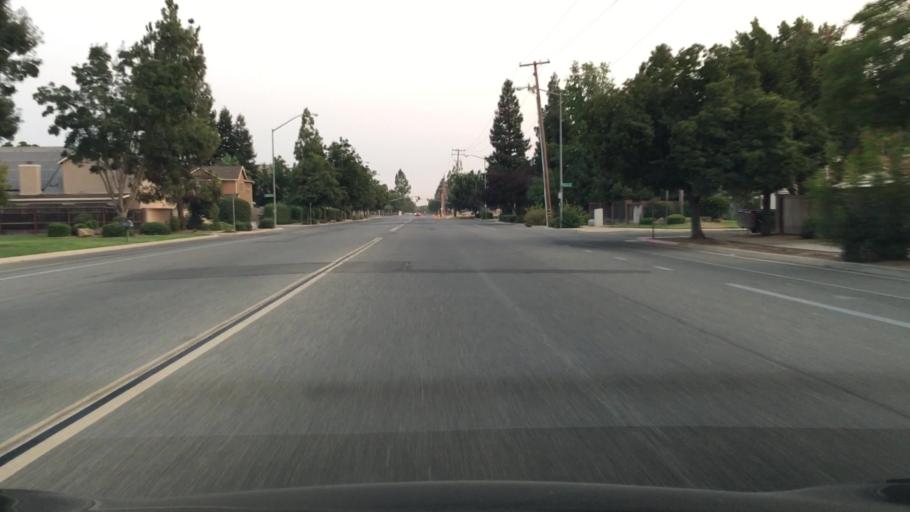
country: US
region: California
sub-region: Fresno County
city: Clovis
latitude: 36.8554
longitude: -119.7478
